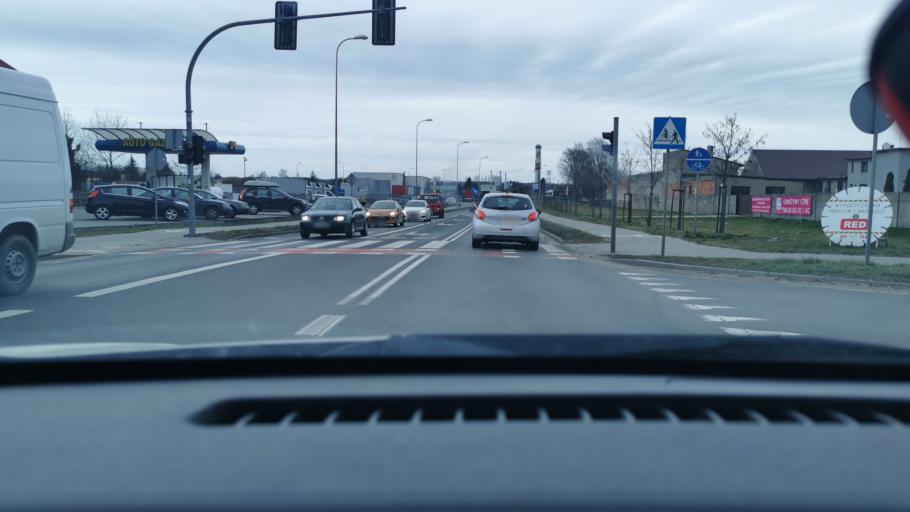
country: PL
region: Greater Poland Voivodeship
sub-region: Powiat ostrowski
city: Ostrow Wielkopolski
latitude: 51.6533
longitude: 17.8385
